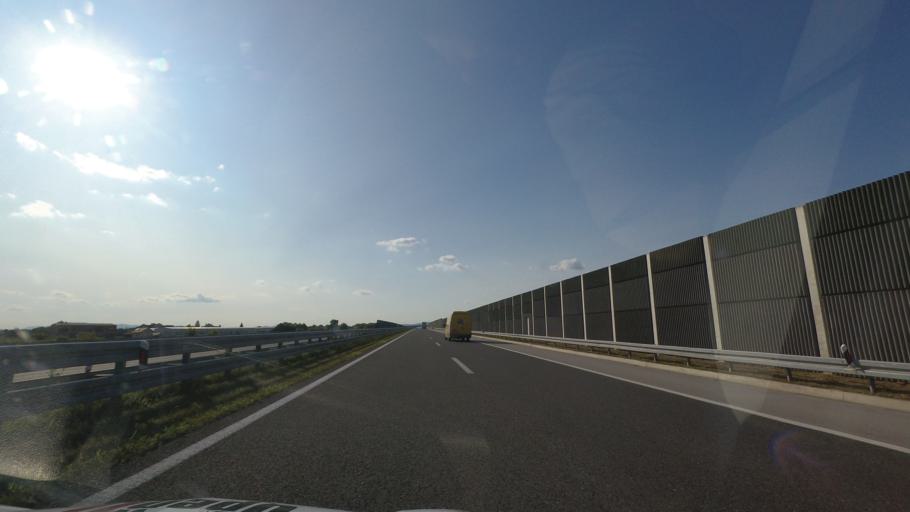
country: HR
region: Zagrebacka
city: Gradici
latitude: 45.7041
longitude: 16.0521
